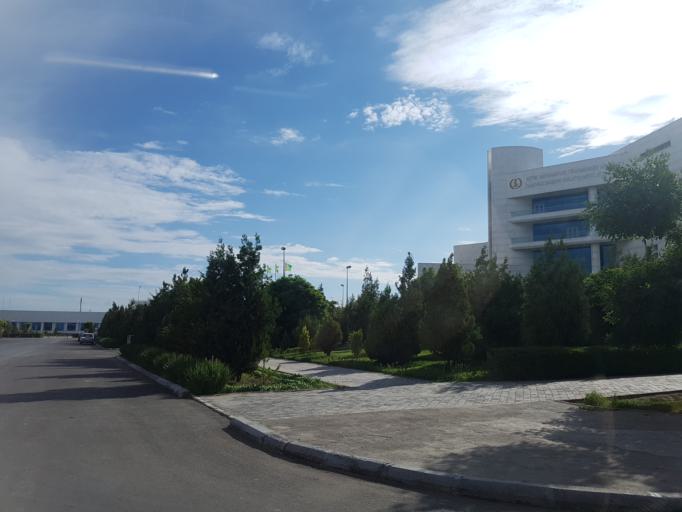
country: TM
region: Dasoguz
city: Dasoguz
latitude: 41.8401
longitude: 59.9452
